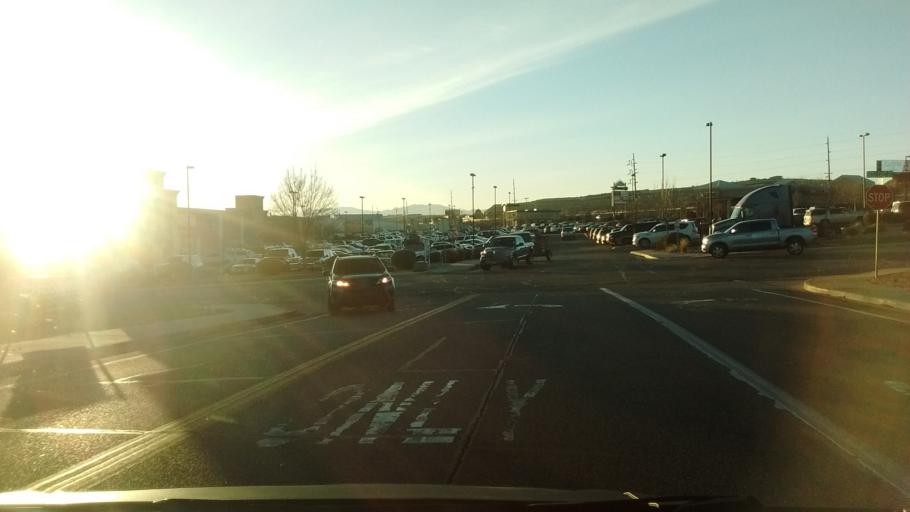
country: US
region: Utah
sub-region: Washington County
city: Washington
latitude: 37.1229
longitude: -113.5314
